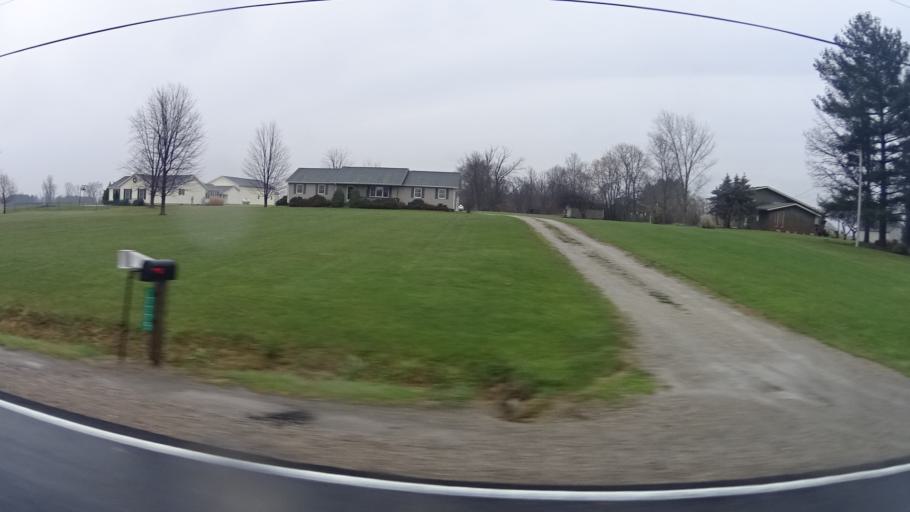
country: US
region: Ohio
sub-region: Lorain County
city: Lagrange
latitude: 41.2252
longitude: -82.1578
